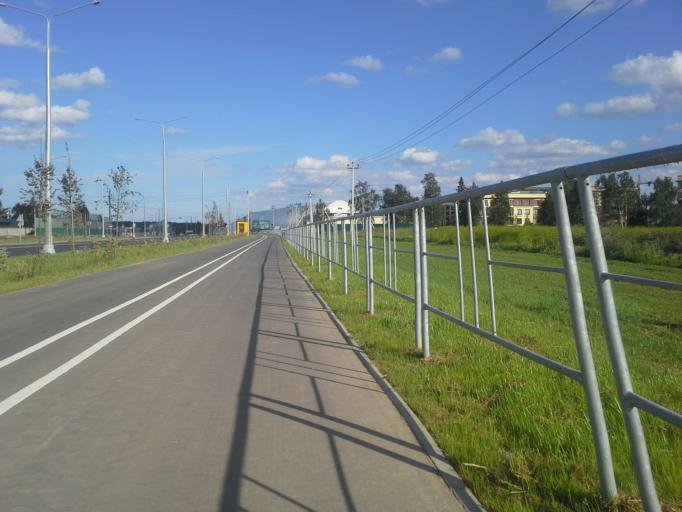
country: RU
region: Moskovskaya
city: Kokoshkino
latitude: 55.5415
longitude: 37.1801
